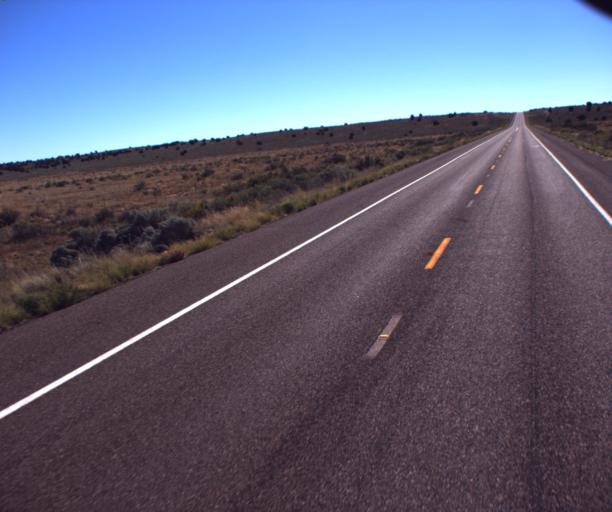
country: US
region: Arizona
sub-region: Navajo County
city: Snowflake
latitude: 34.6671
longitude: -109.7214
